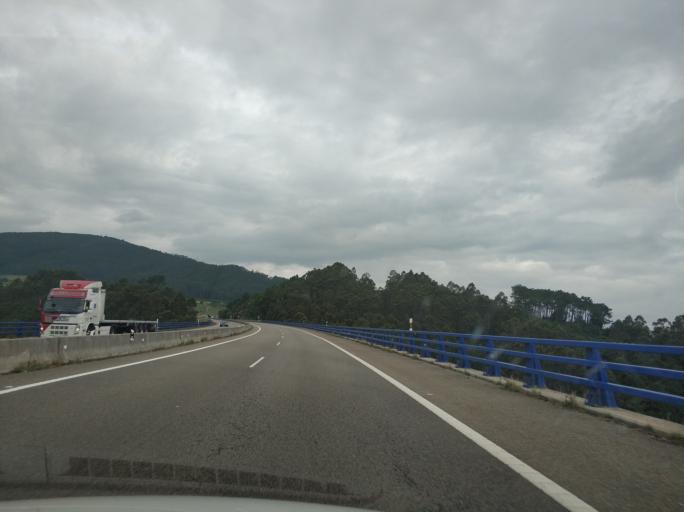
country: ES
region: Asturias
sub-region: Province of Asturias
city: Navia
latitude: 43.5323
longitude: -6.7330
